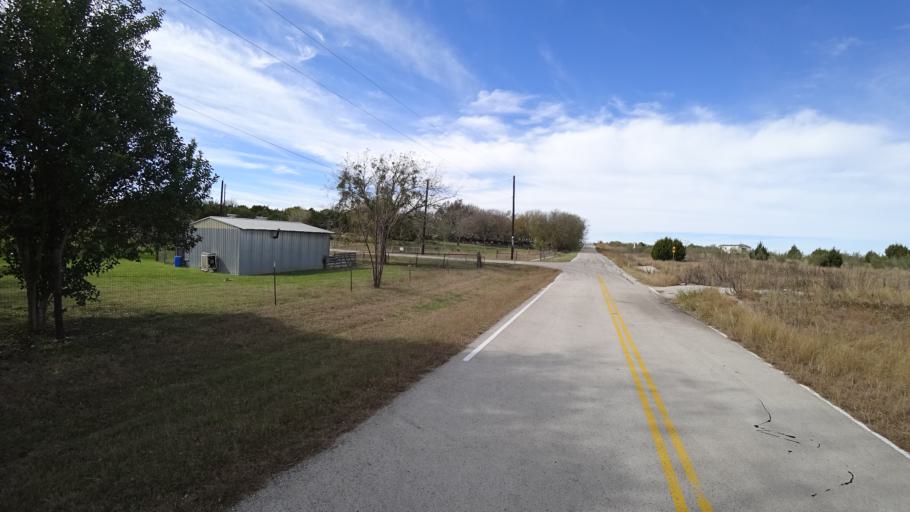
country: US
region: Texas
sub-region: Travis County
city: Onion Creek
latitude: 30.1253
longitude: -97.7312
